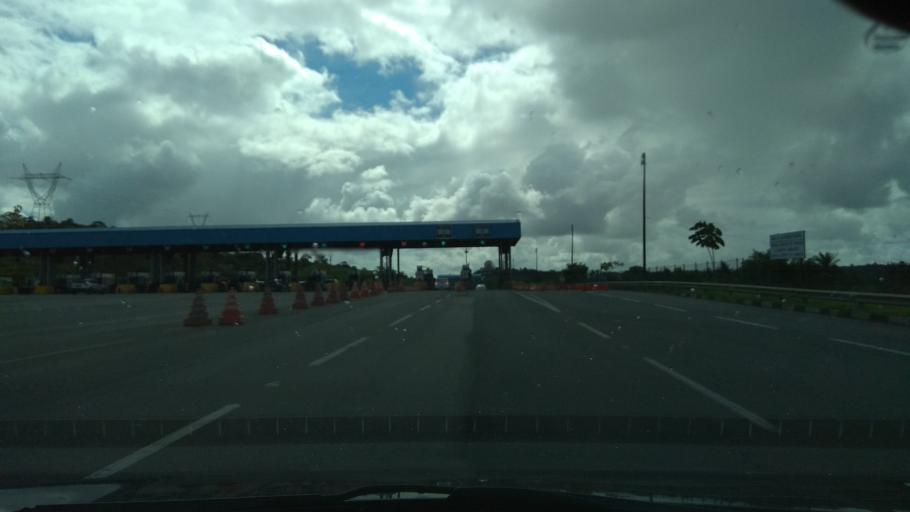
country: BR
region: Bahia
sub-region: Simoes Filho
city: Simoes Filho
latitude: -12.7517
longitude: -38.4306
